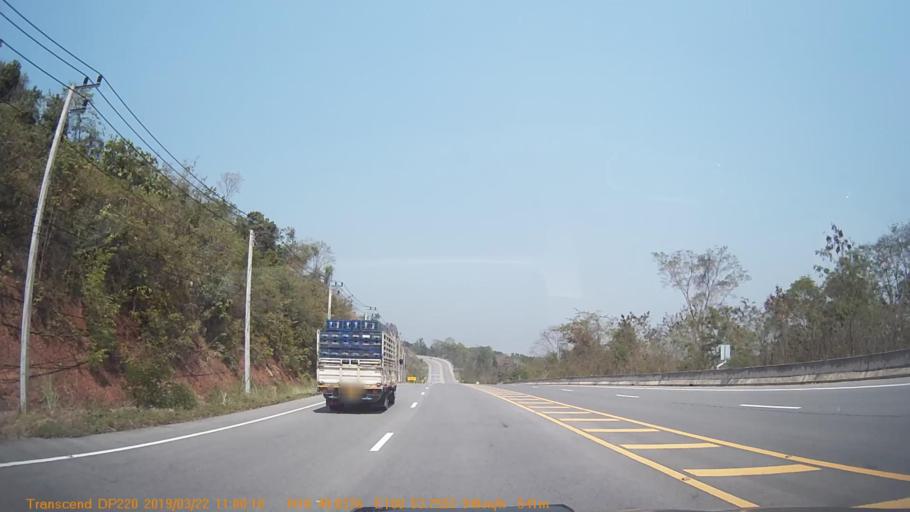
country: TH
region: Phetchabun
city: Khao Kho
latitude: 16.8309
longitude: 100.8958
